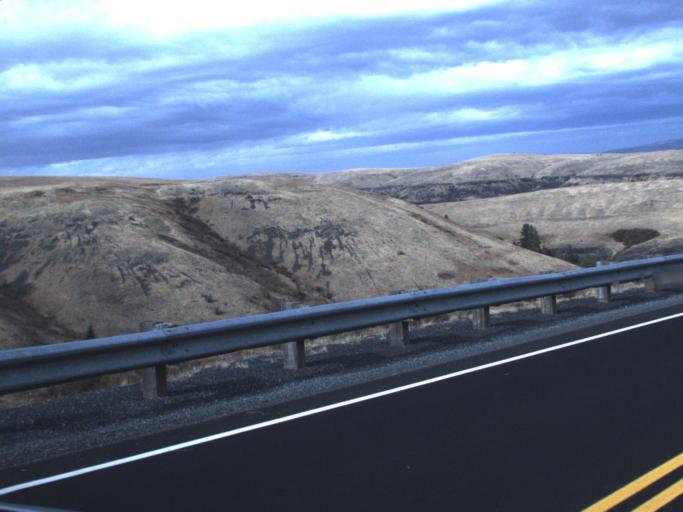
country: US
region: Washington
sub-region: Okanogan County
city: Coulee Dam
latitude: 47.8630
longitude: -118.7246
